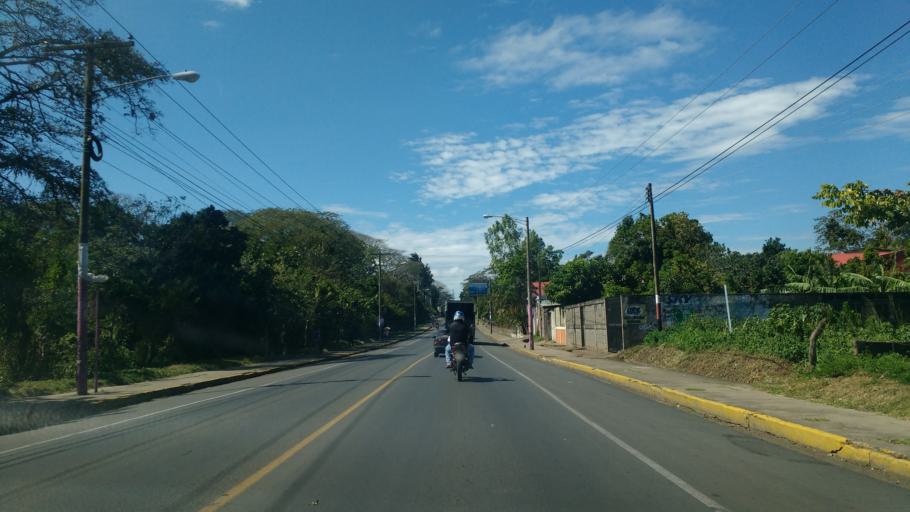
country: NI
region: Carazo
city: Jinotepe
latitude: 11.8531
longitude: -86.2064
